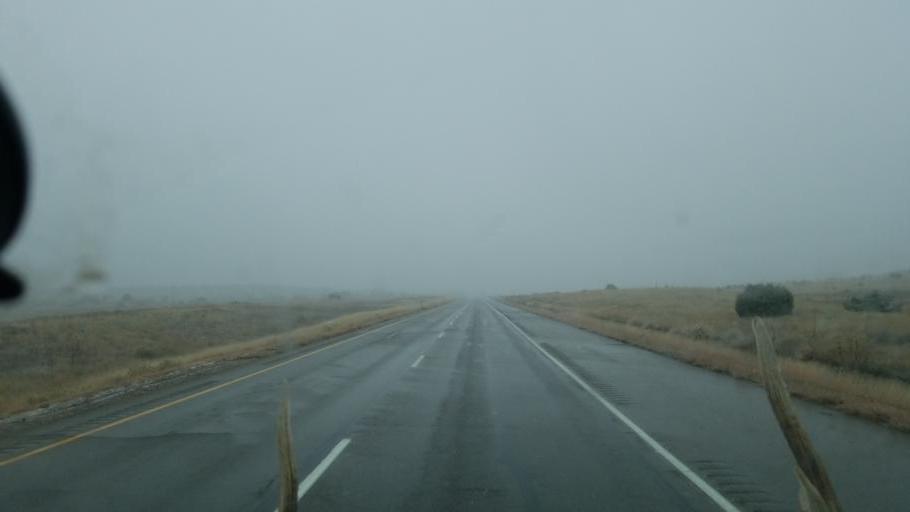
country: US
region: Colorado
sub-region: Pueblo County
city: Colorado City
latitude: 38.0489
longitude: -104.7241
